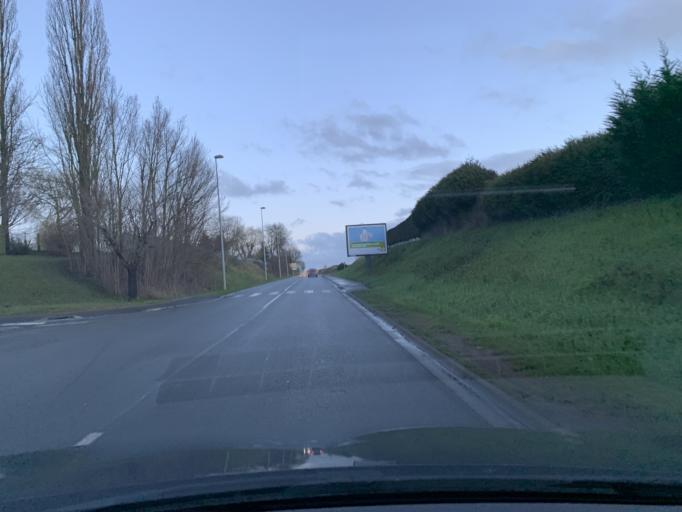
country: FR
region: Nord-Pas-de-Calais
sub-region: Departement du Nord
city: Cambrai
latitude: 50.1561
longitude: 3.2587
